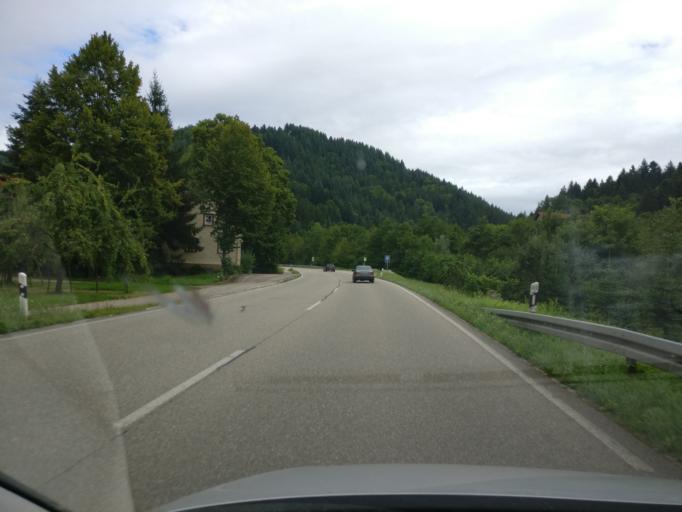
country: DE
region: Baden-Wuerttemberg
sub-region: Freiburg Region
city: Lautenbach
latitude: 48.5102
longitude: 8.1319
